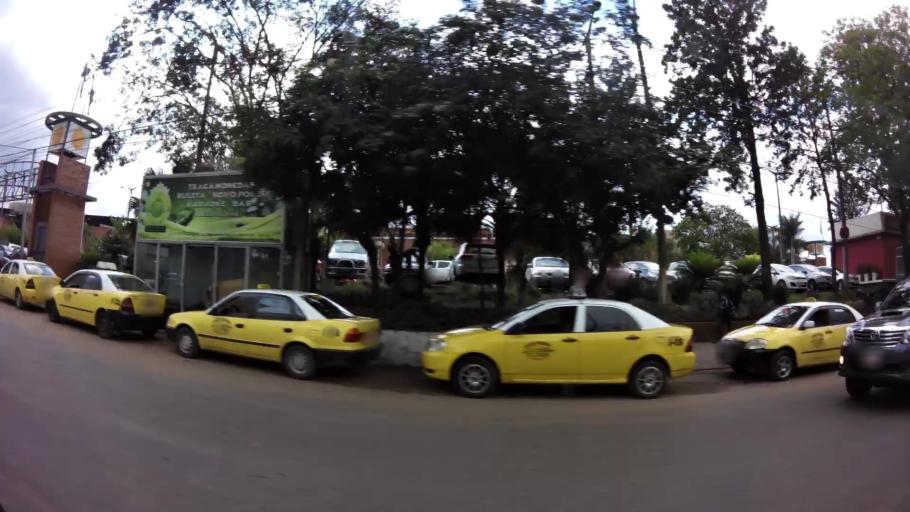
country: PY
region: Central
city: Fernando de la Mora
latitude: -25.2836
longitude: -57.5662
